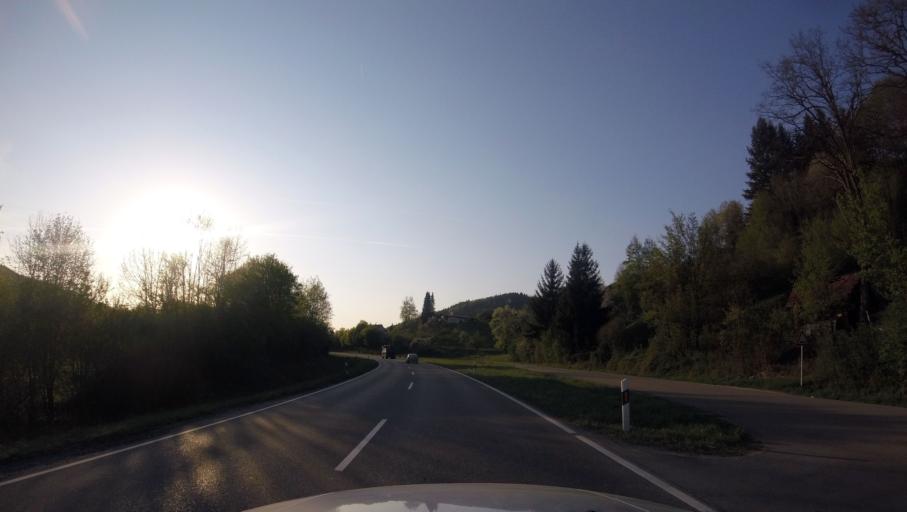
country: DE
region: Baden-Wuerttemberg
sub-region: Regierungsbezirk Stuttgart
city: Murrhardt
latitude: 48.9877
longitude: 9.5589
